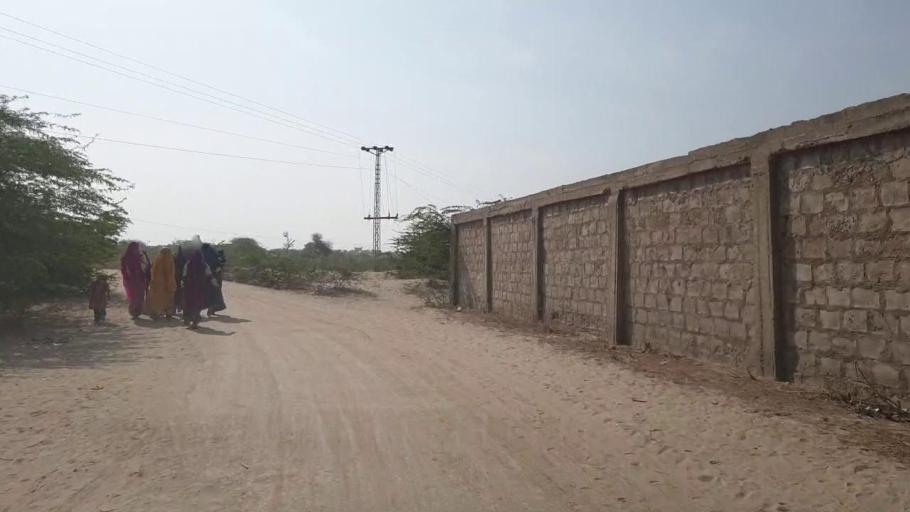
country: PK
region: Sindh
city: Umarkot
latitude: 25.3351
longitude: 69.7342
